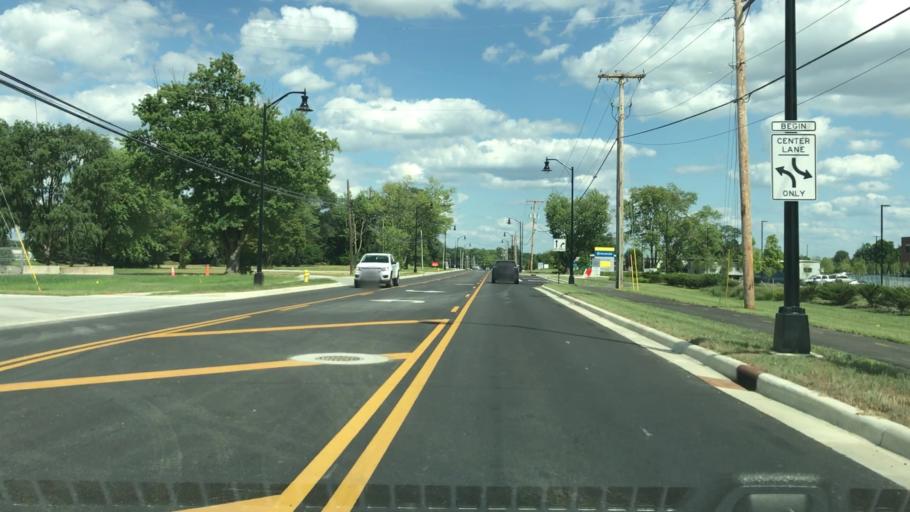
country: US
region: Ohio
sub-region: Franklin County
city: Grove City
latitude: 39.8775
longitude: -83.0346
